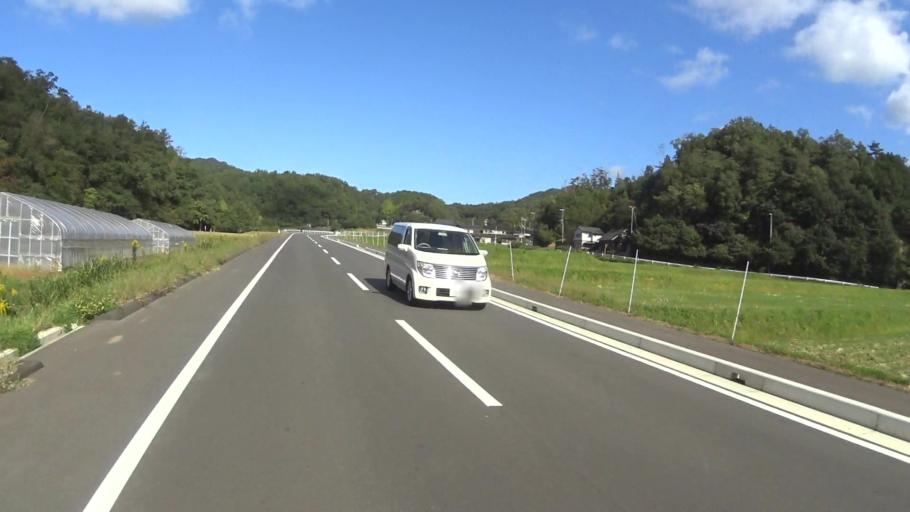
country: JP
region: Kyoto
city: Miyazu
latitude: 35.6130
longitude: 135.1322
